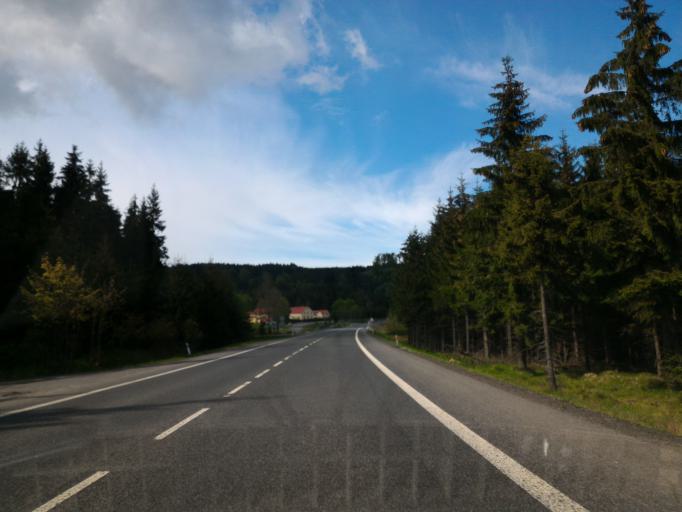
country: CZ
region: Ustecky
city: Dolni Podluzi
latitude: 50.8279
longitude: 14.5910
